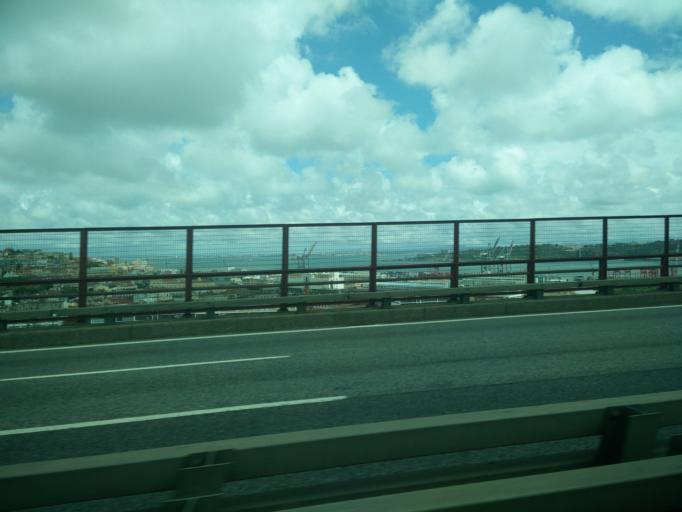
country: PT
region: Setubal
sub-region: Almada
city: Pragal
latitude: 38.7063
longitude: -9.1787
